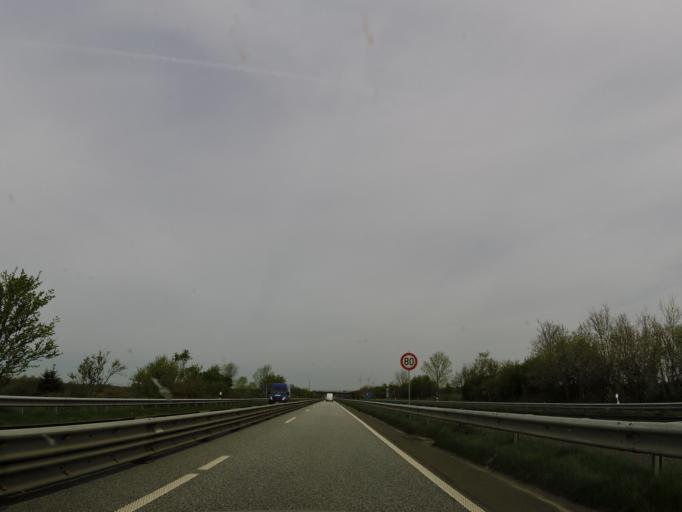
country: DE
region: Schleswig-Holstein
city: Tensbuttel-Rost
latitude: 54.1067
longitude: 9.2633
